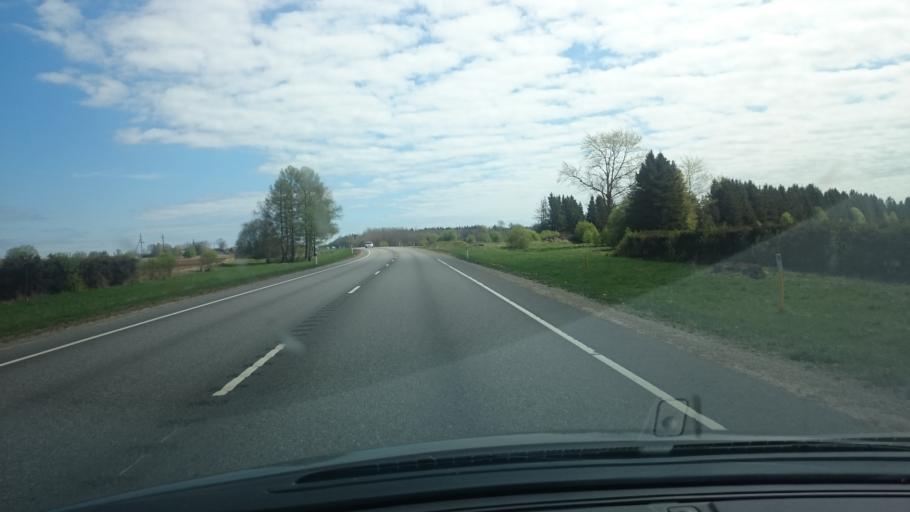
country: EE
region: Ida-Virumaa
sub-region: Kohtla-Nomme vald
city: Kohtla-Nomme
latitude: 59.4213
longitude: 27.1971
